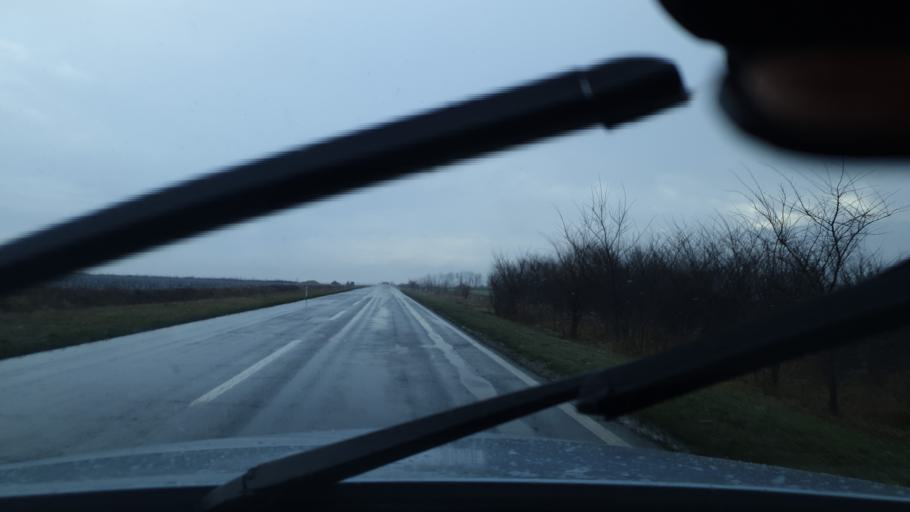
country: RS
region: Autonomna Pokrajina Vojvodina
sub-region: Juznobanatski Okrug
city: Pancevo
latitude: 44.8469
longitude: 20.7817
